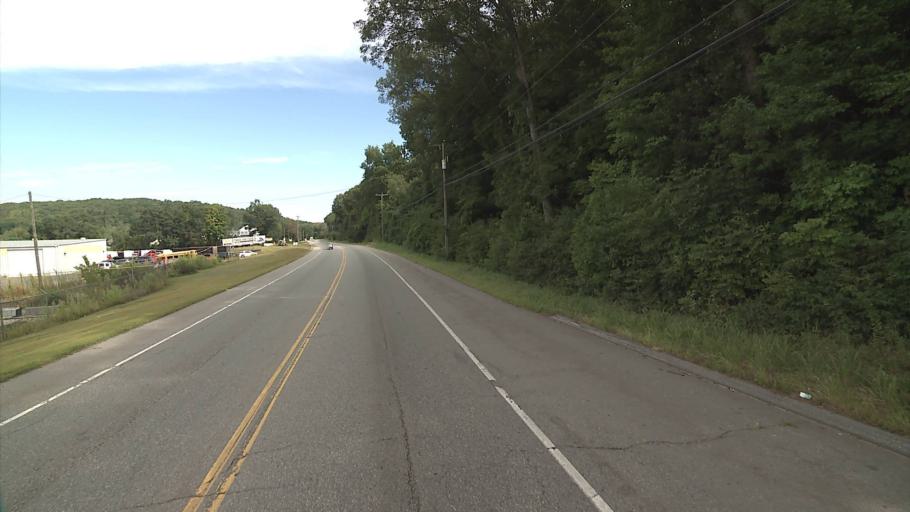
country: US
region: Connecticut
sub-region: New London County
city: Baltic
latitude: 41.5779
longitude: -72.1317
